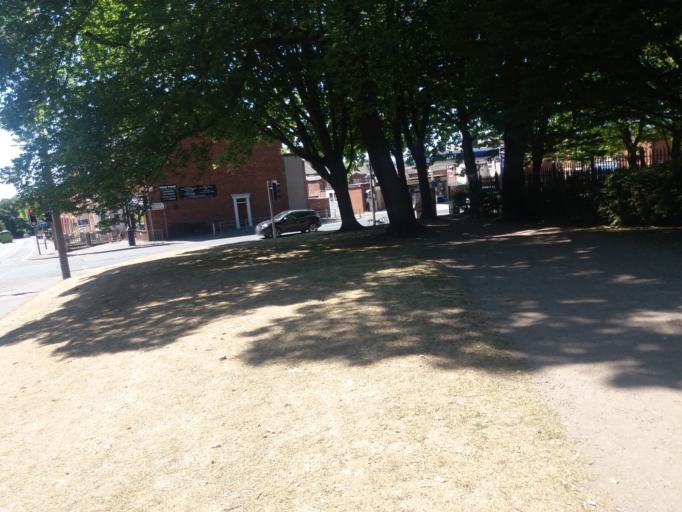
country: GB
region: England
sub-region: Lancashire
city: Preston
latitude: 53.7568
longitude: -2.7098
